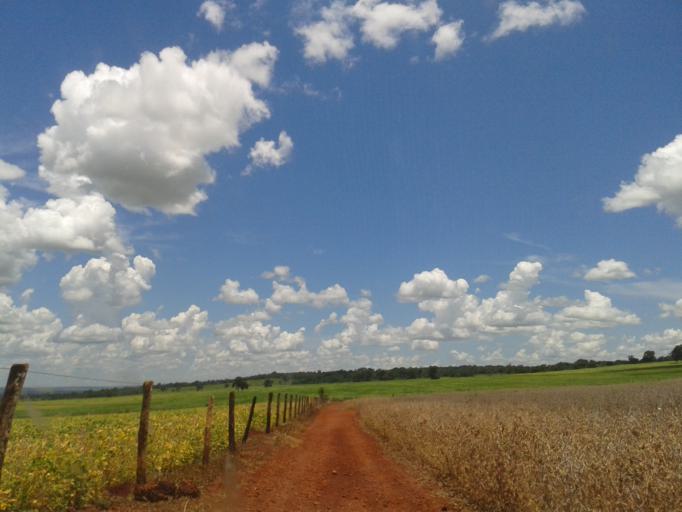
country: BR
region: Minas Gerais
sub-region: Capinopolis
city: Capinopolis
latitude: -18.7625
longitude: -49.7943
